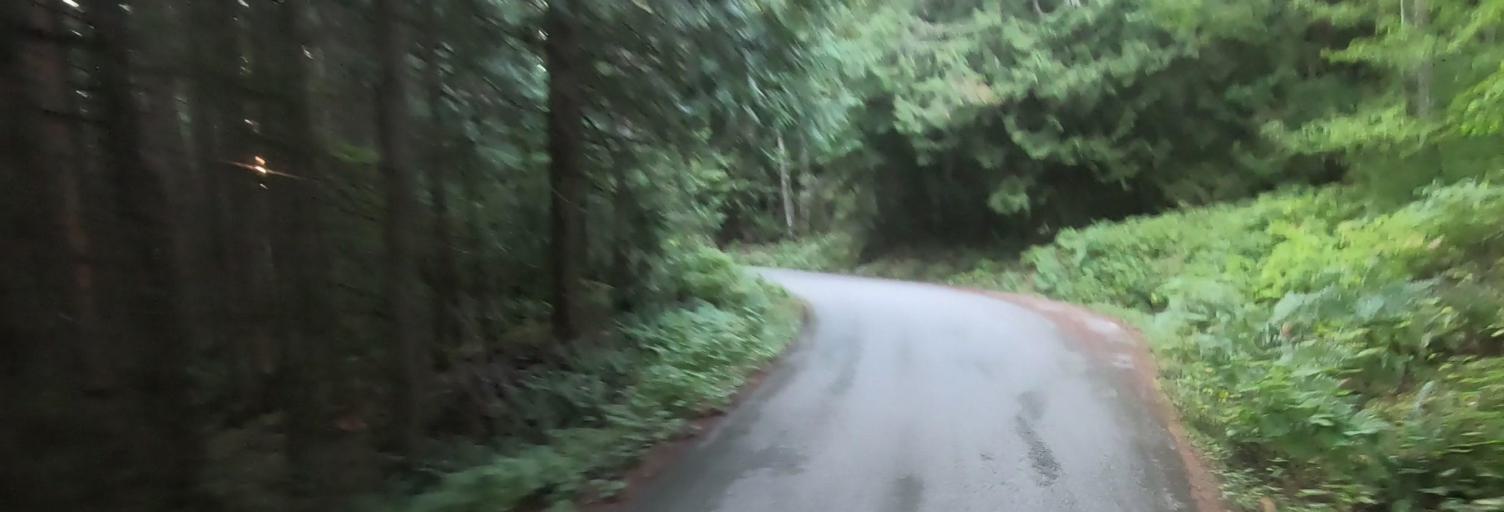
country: US
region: Washington
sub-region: Whatcom County
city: Peaceful Valley
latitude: 48.9012
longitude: -121.9281
